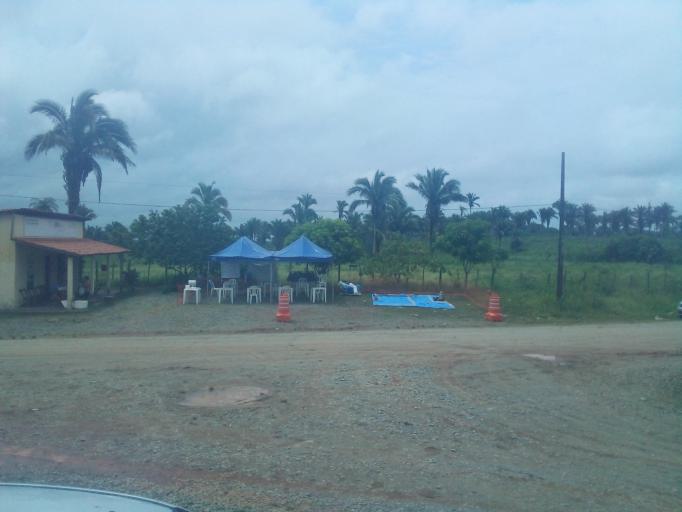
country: BR
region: Maranhao
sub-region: Vitoria Do Mearim
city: Vitoria do Mearim
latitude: -3.5328
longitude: -44.8621
